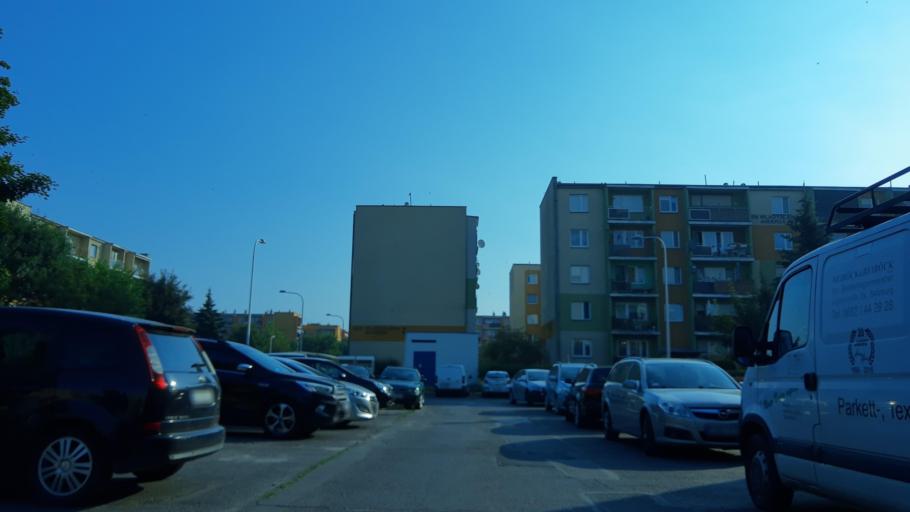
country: PL
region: Lodz Voivodeship
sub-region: Powiat sieradzki
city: Sieradz
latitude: 51.5868
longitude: 18.7116
